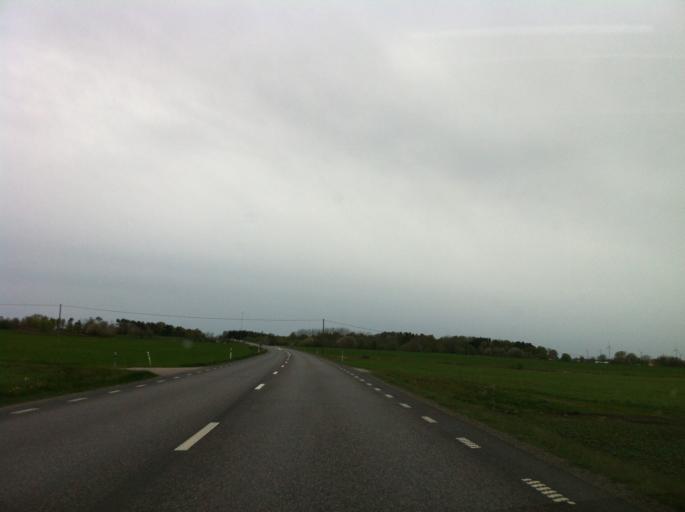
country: SE
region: Halland
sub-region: Falkenbergs Kommun
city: Falkenberg
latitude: 56.9549
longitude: 12.5405
